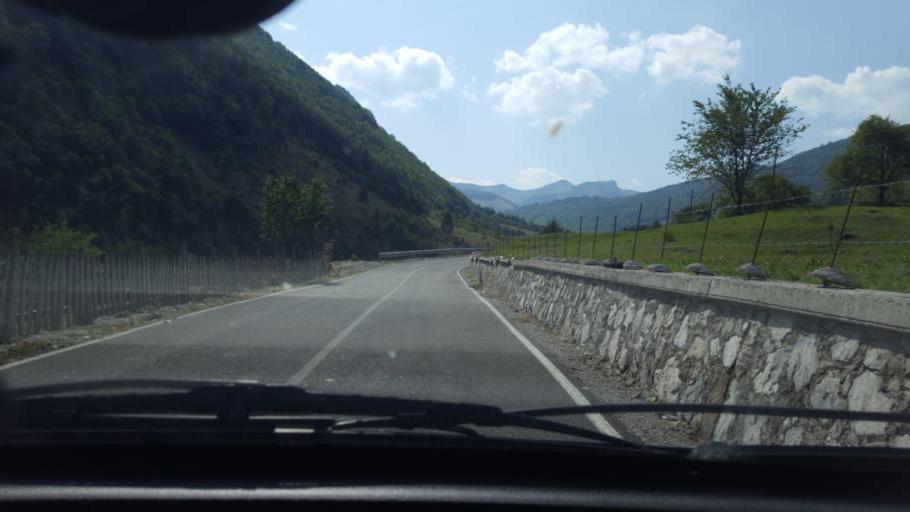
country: ME
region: Andrijevica
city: Andrijevica
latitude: 42.5585
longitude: 19.7308
